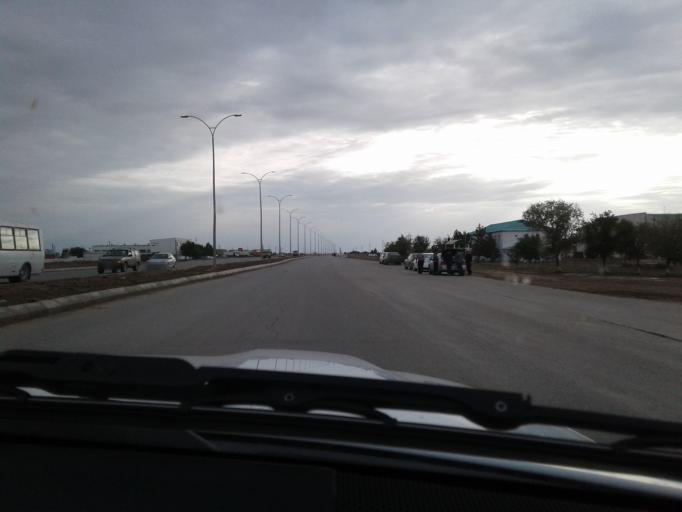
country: TM
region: Ahal
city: Tejen
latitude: 37.3797
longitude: 60.4821
